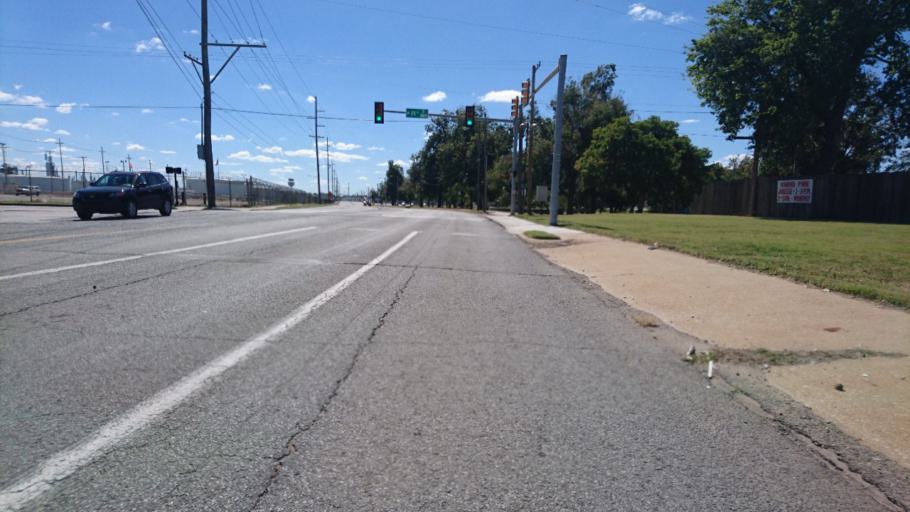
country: US
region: Oklahoma
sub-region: Tulsa County
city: Tulsa
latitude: 36.1266
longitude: -96.0071
